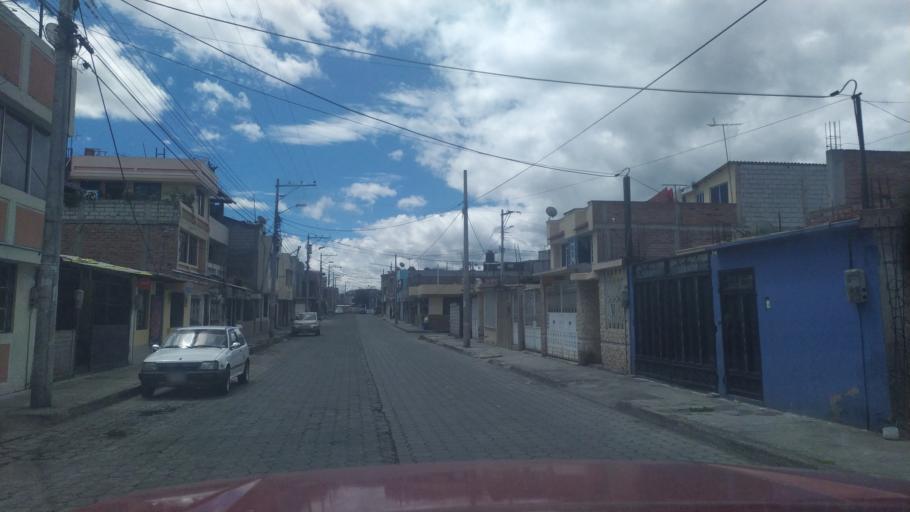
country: EC
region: Chimborazo
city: Riobamba
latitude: -1.6849
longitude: -78.6448
